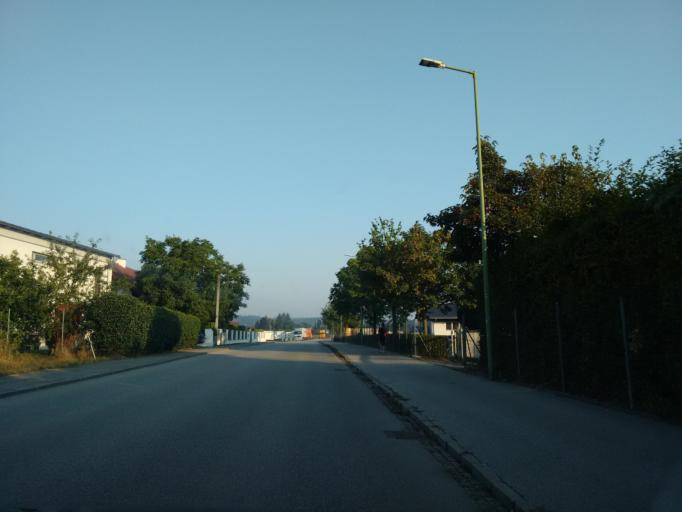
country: AT
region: Upper Austria
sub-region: Wels Stadt
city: Wels
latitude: 48.1771
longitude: 14.0131
